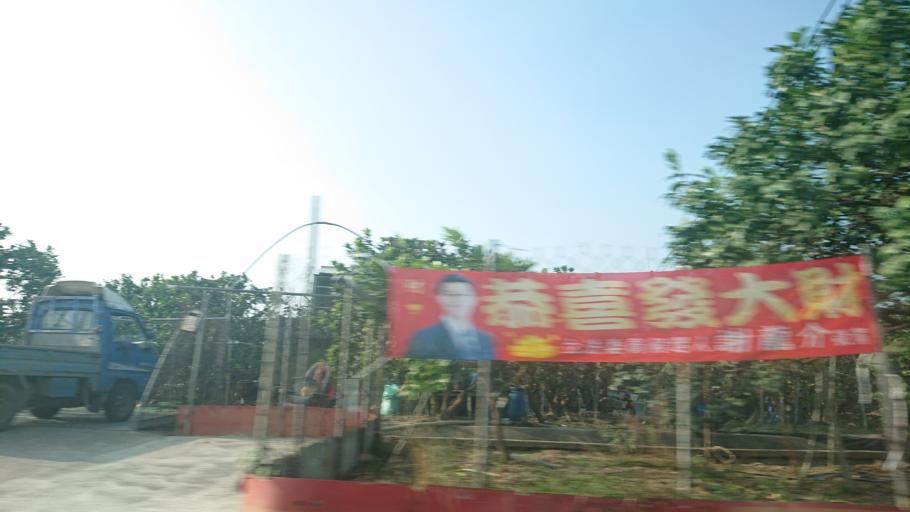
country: TW
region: Taiwan
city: Xinying
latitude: 23.1818
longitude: 120.2661
